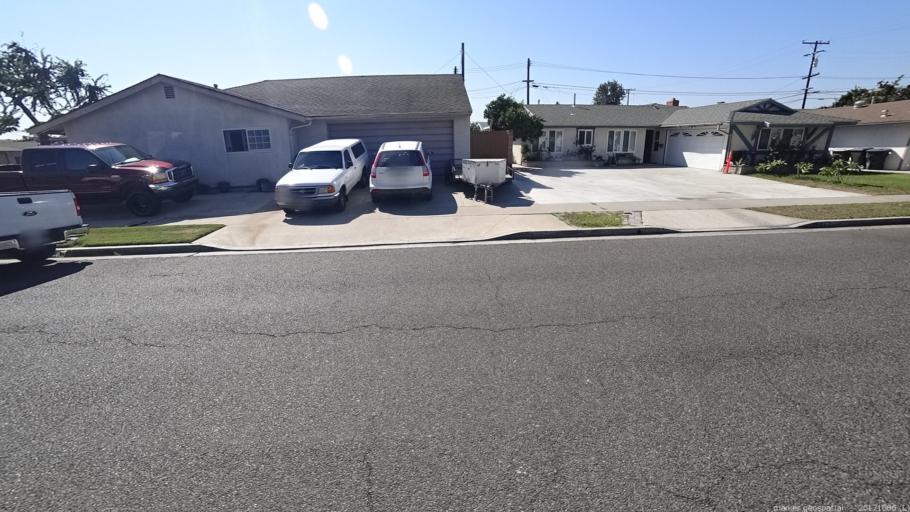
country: US
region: California
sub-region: Orange County
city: Stanton
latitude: 33.7910
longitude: -118.0192
